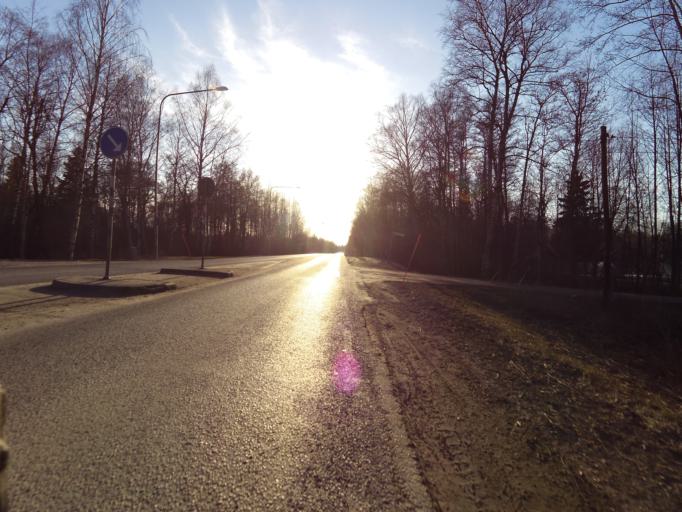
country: SE
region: Gaevleborg
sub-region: Gavle Kommun
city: Gavle
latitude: 60.6745
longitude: 17.2032
